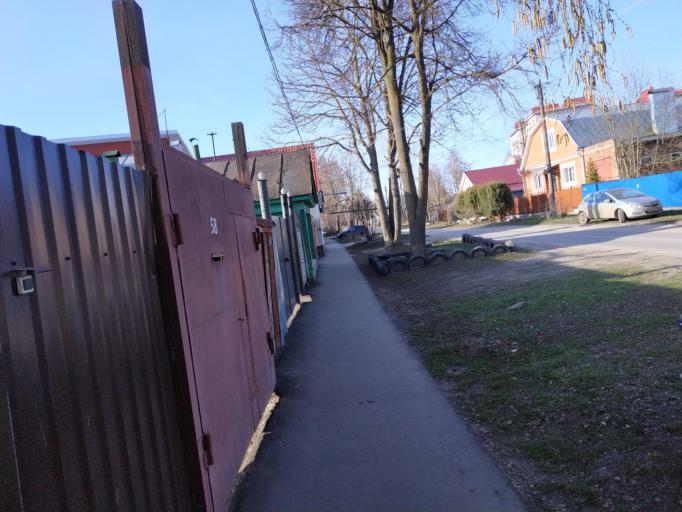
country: RU
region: Nizjnij Novgorod
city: Arzamas
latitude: 55.3957
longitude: 43.8145
